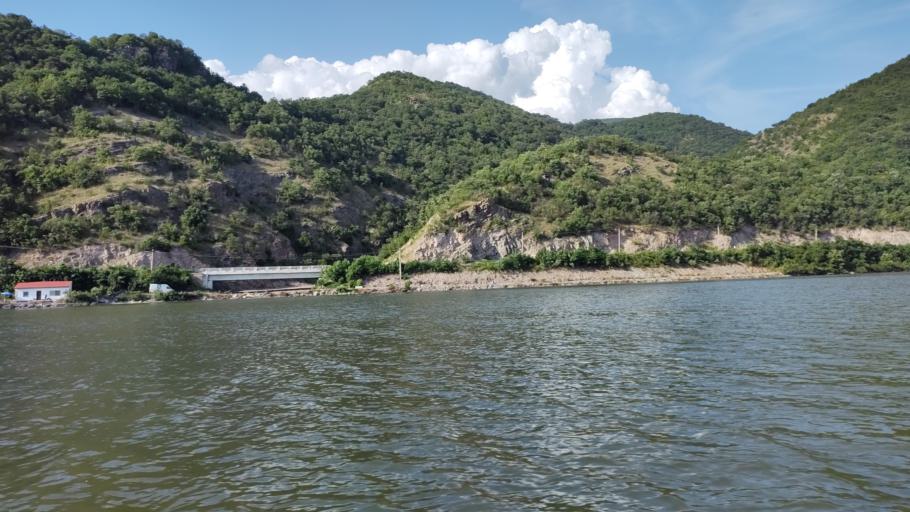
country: RO
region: Mehedinti
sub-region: Comuna Svinita
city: Svinita
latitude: 44.5456
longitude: 22.0428
